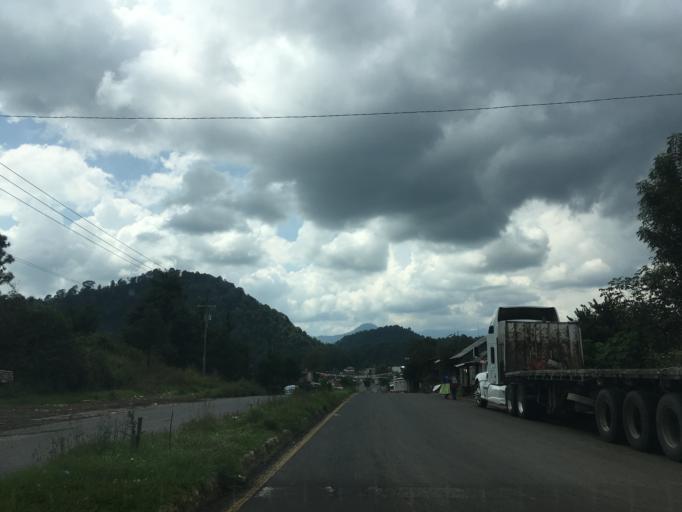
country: MX
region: Michoacan
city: Capacuaro
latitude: 19.5253
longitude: -102.1041
